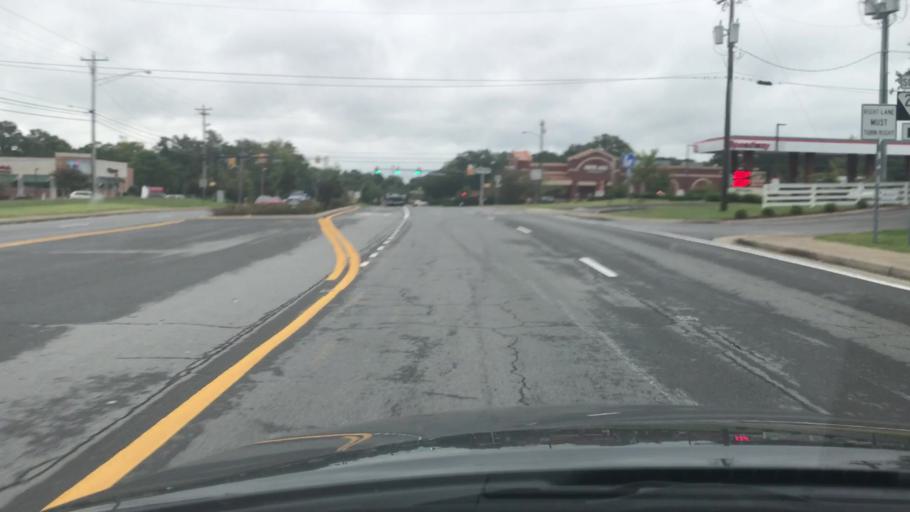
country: US
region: Tennessee
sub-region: Sumner County
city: White House
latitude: 36.4688
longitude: -86.6668
